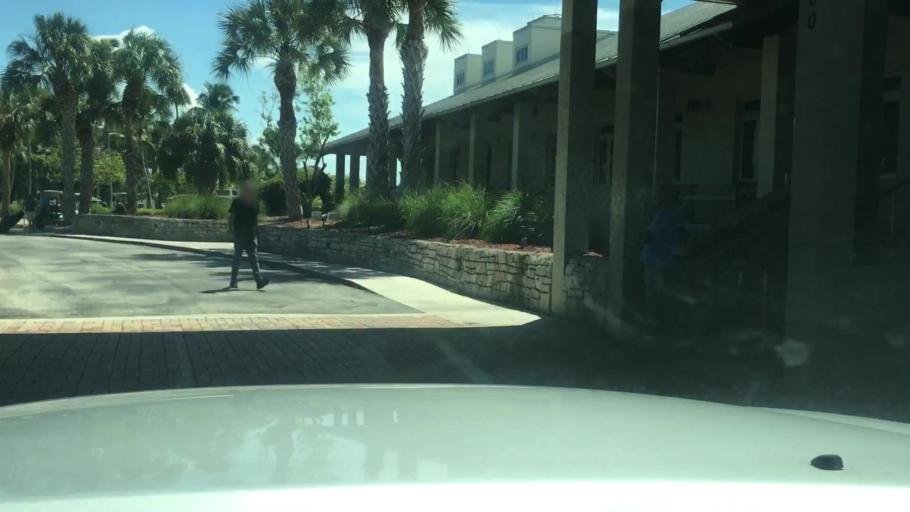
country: US
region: Florida
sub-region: Miami-Dade County
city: Key Biscayne
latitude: 25.7164
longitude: -80.1592
